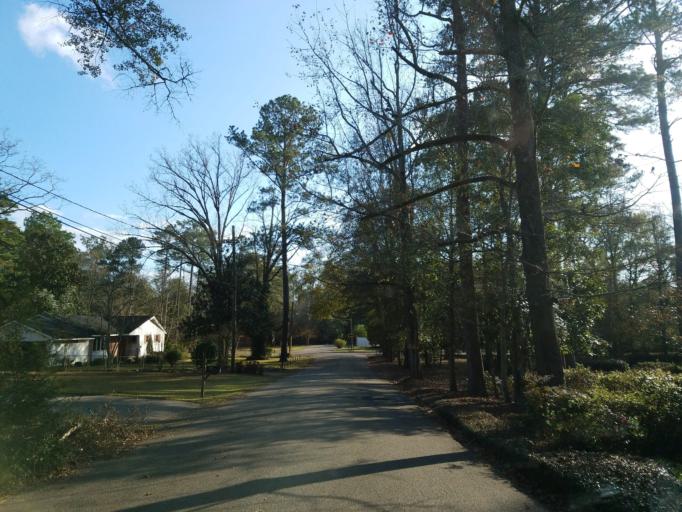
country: US
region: Mississippi
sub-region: Lamar County
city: West Hattiesburg
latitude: 31.3184
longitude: -89.3437
